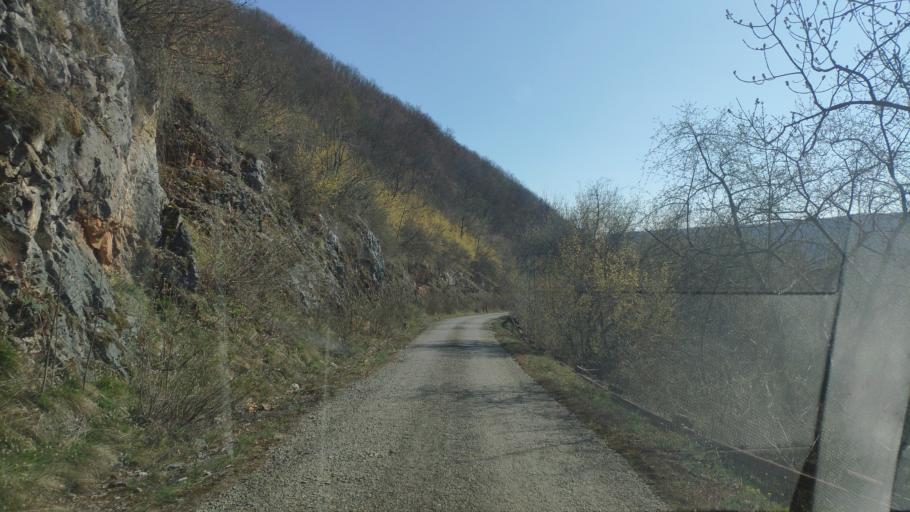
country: SK
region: Kosicky
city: Roznava
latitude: 48.5716
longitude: 20.4055
